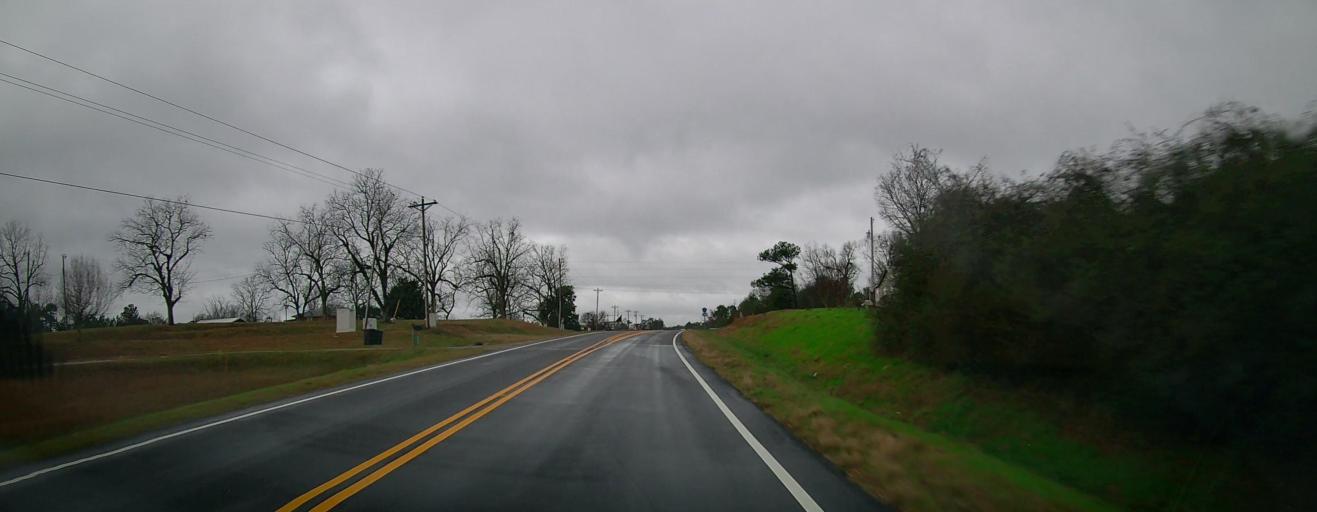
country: US
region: Alabama
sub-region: Chilton County
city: Thorsby
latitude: 32.7890
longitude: -86.9041
